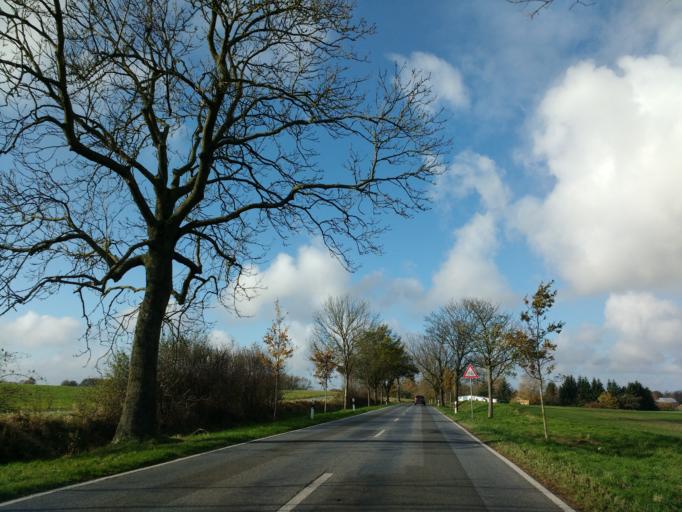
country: DE
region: Mecklenburg-Vorpommern
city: Ostseebad Boltenhagen
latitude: 53.9592
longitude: 11.2049
